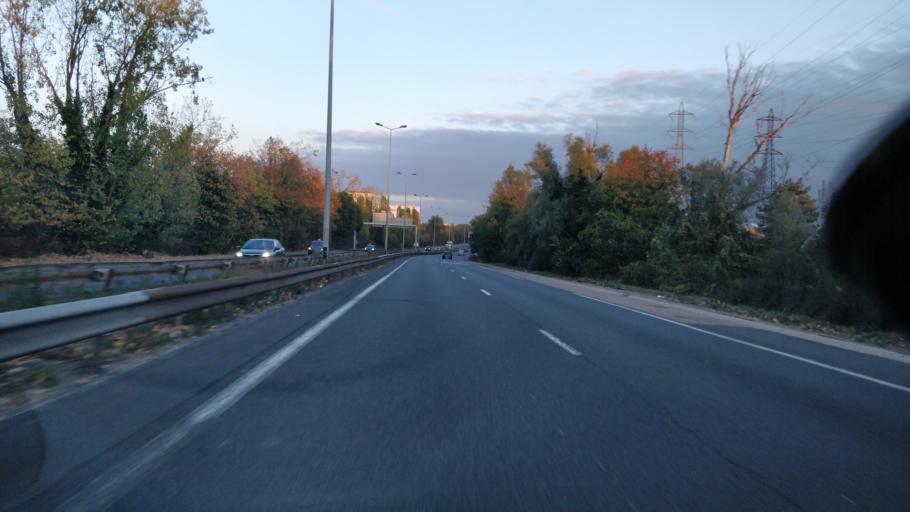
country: FR
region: Ile-de-France
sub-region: Departement de Seine-Saint-Denis
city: Noisy-le-Sec
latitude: 48.8866
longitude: 2.4809
